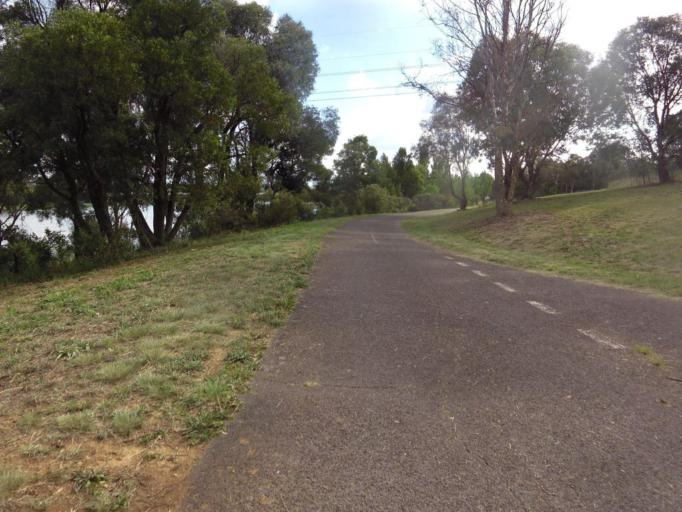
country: AU
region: Australian Capital Territory
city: Belconnen
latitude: -35.2260
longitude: 149.0781
